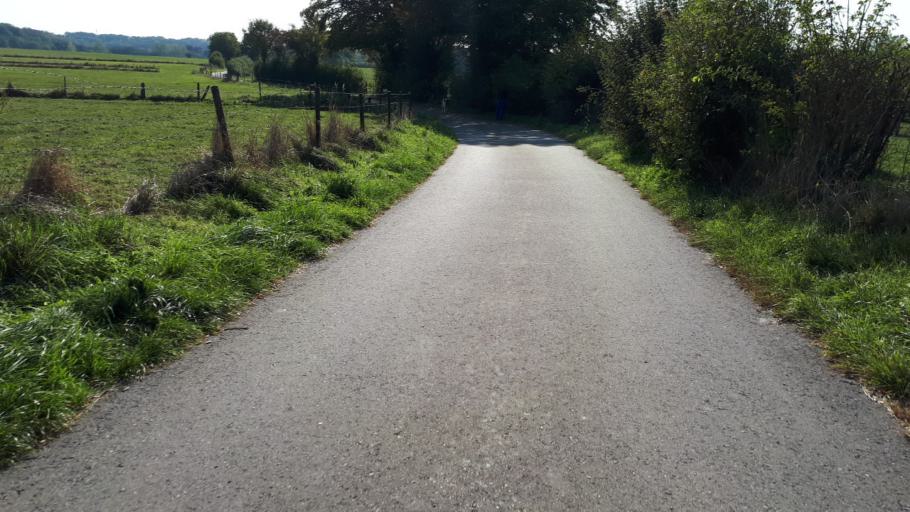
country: LU
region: Luxembourg
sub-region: Canton de Capellen
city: Kehlen
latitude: 49.6611
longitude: 6.0310
